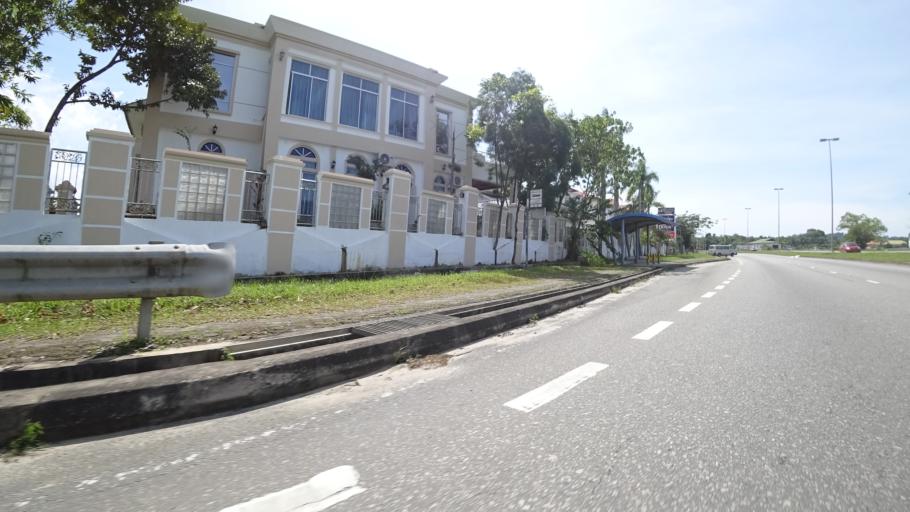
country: BN
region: Brunei and Muara
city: Bandar Seri Begawan
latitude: 4.8951
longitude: 114.8516
